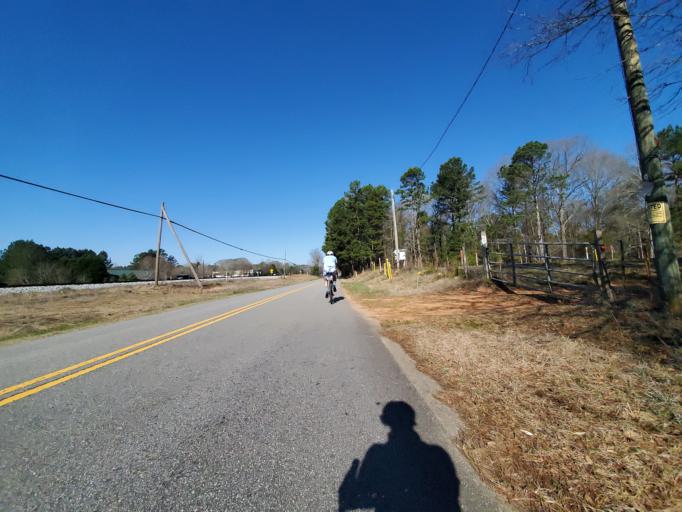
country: US
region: Georgia
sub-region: Clarke County
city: Country Club Estates
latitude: 33.9922
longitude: -83.4334
